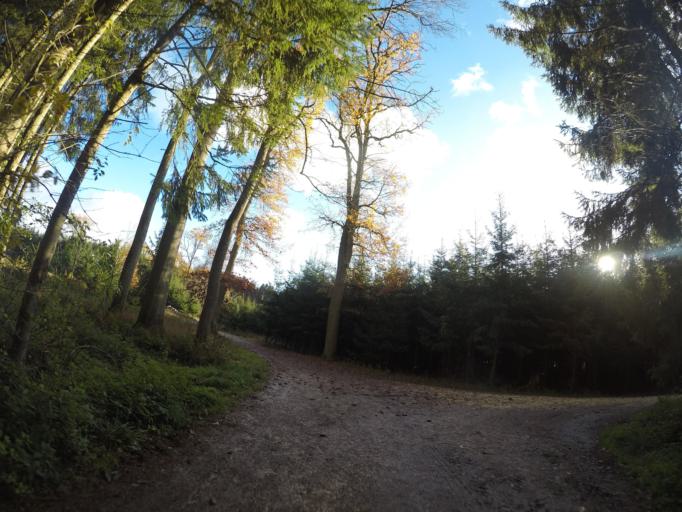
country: DE
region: Baden-Wuerttemberg
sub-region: Tuebingen Region
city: Beimerstetten
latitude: 48.4562
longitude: 10.0121
